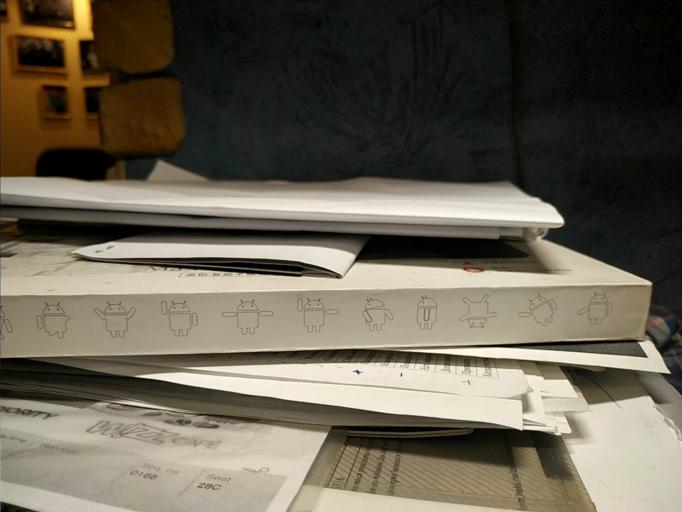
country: RU
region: Tverskaya
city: Zubtsov
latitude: 56.0814
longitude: 34.7957
